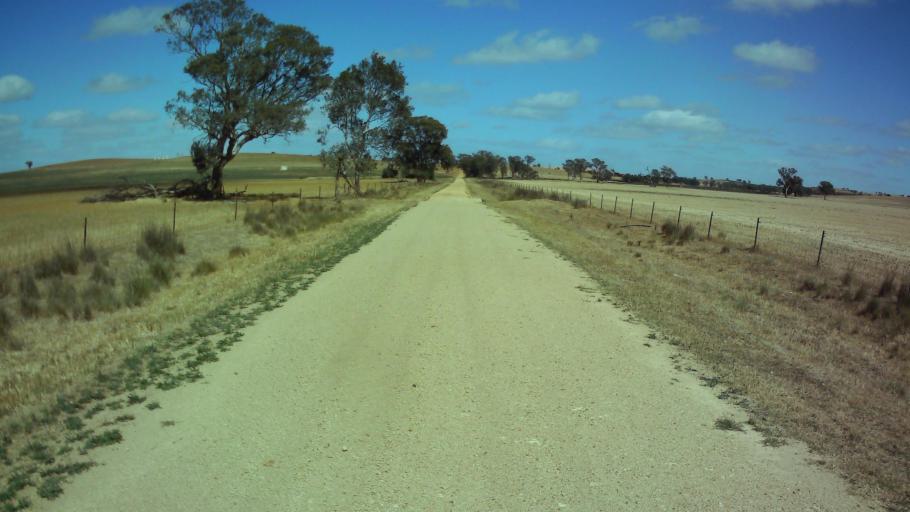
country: AU
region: New South Wales
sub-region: Weddin
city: Grenfell
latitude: -33.9836
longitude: 148.4027
